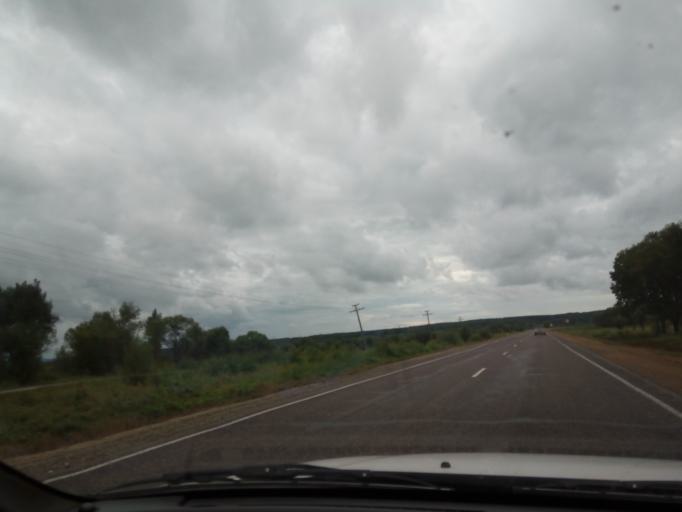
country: RU
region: Primorskiy
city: Dal'nerechensk
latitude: 45.9057
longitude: 133.7537
